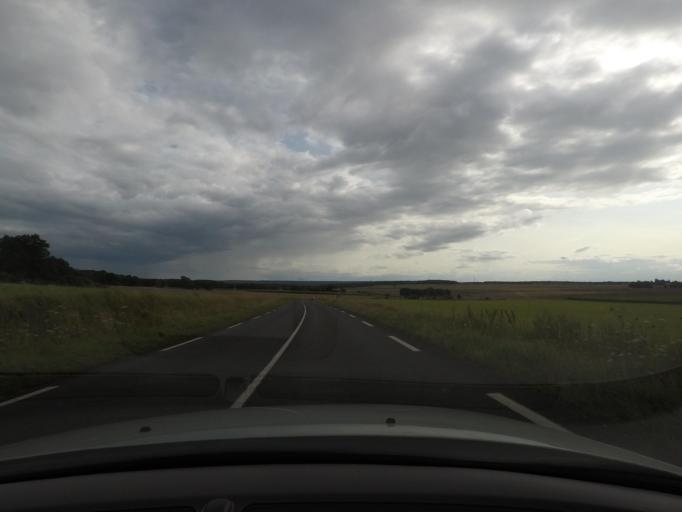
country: FR
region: Haute-Normandie
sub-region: Departement de la Seine-Maritime
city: Ymare
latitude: 49.3488
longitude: 1.1636
